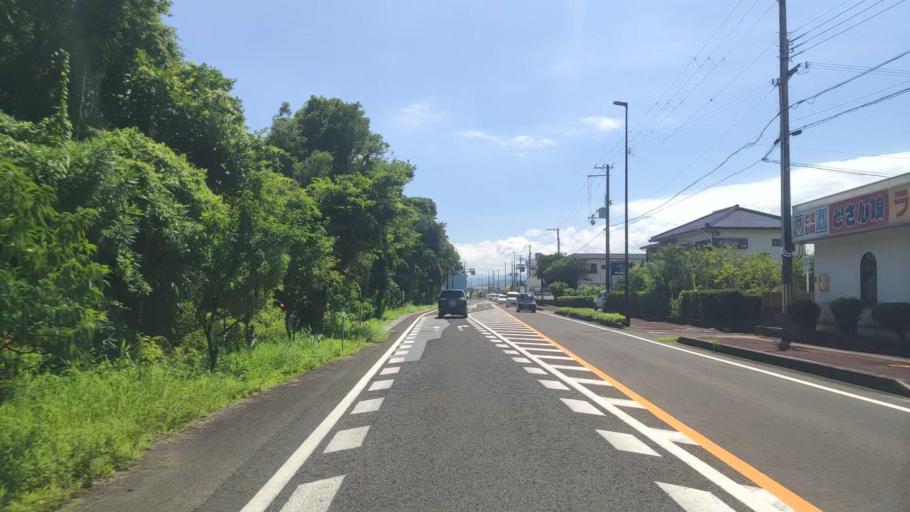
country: JP
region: Wakayama
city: Shingu
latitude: 33.8757
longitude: 136.0893
